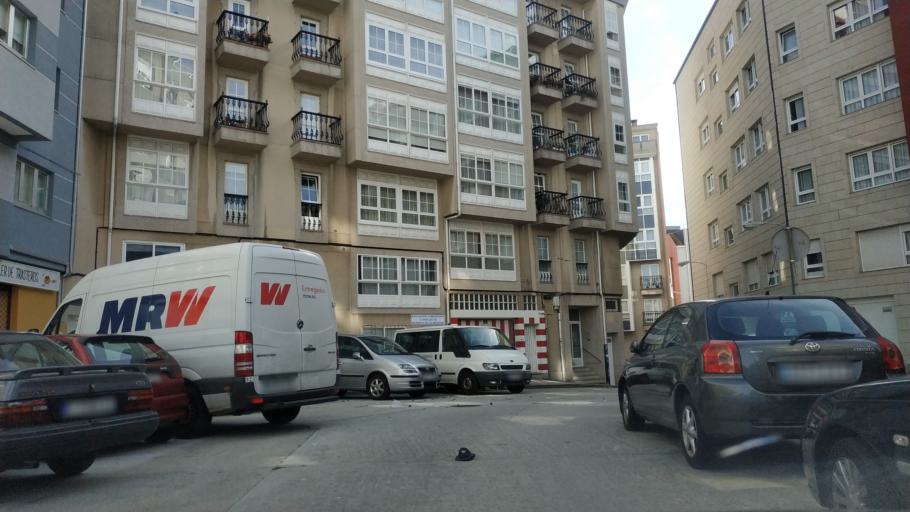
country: ES
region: Galicia
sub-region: Provincia da Coruna
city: A Coruna
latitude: 43.3753
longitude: -8.3960
